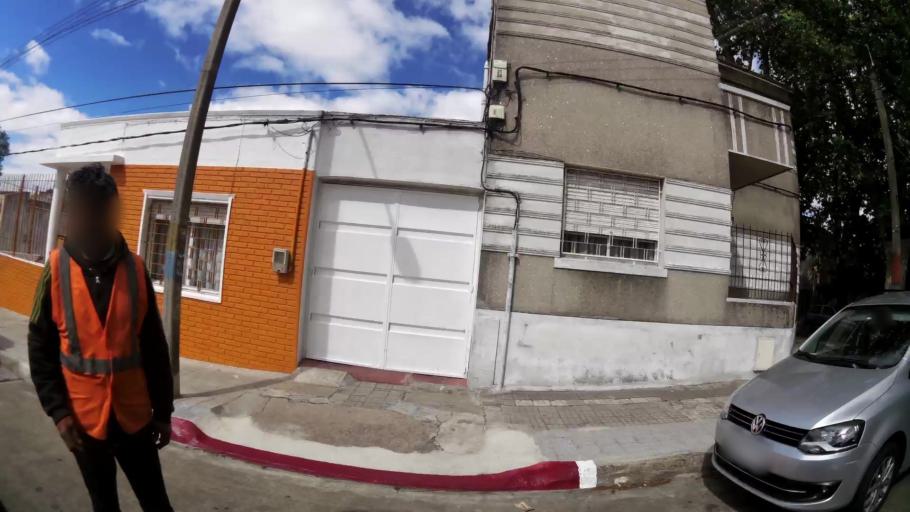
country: UY
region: Montevideo
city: Montevideo
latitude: -34.8765
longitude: -56.1395
